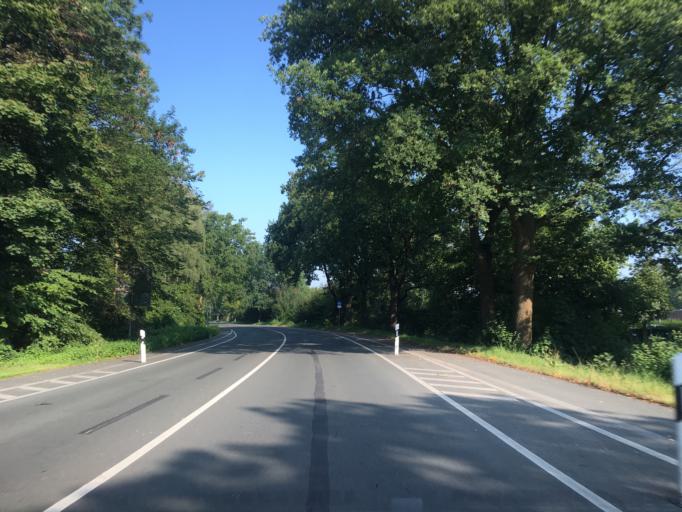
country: DE
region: North Rhine-Westphalia
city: Selm
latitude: 51.6974
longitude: 7.4655
